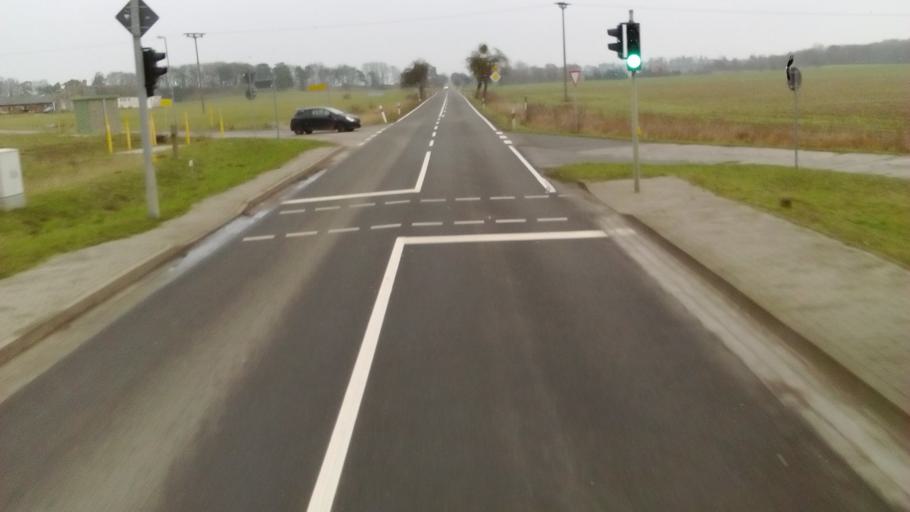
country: DE
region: Brandenburg
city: Goritz
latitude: 53.4871
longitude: 13.8628
